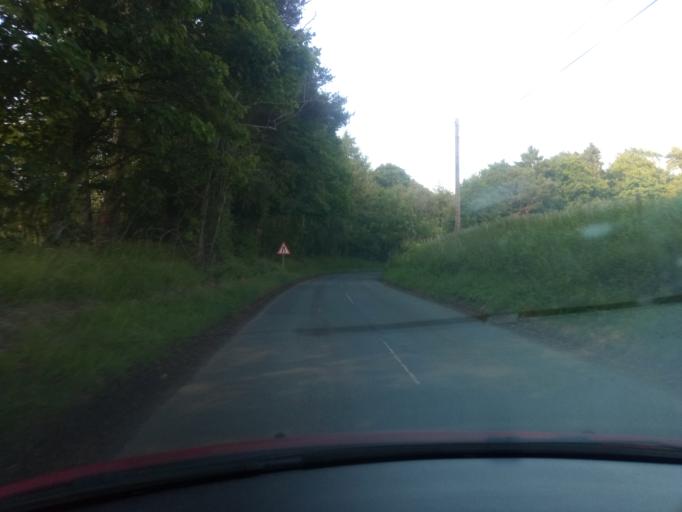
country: GB
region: Scotland
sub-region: The Scottish Borders
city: Selkirk
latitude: 55.5168
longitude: -2.9252
